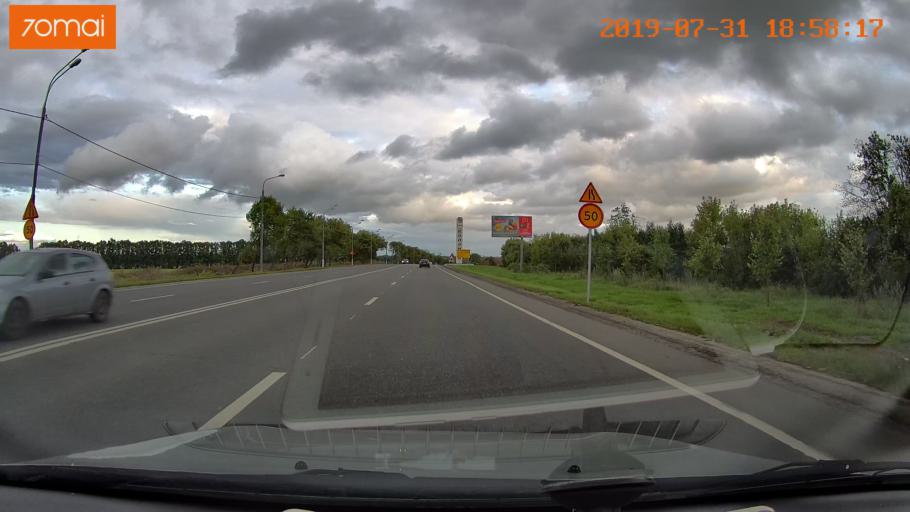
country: RU
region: Moskovskaya
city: Raduzhnyy
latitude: 55.1480
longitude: 38.7026
